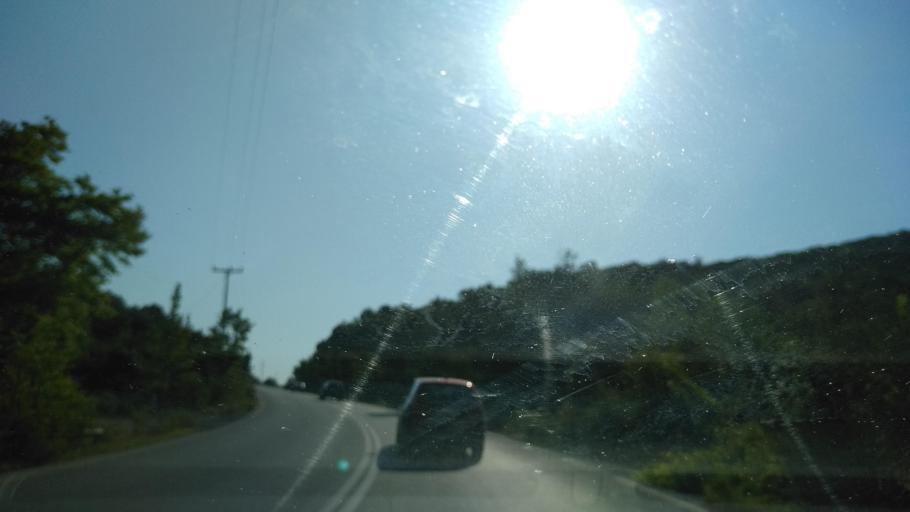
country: GR
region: Central Macedonia
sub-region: Nomos Chalkidikis
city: Stratonion
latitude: 40.5786
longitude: 23.8037
